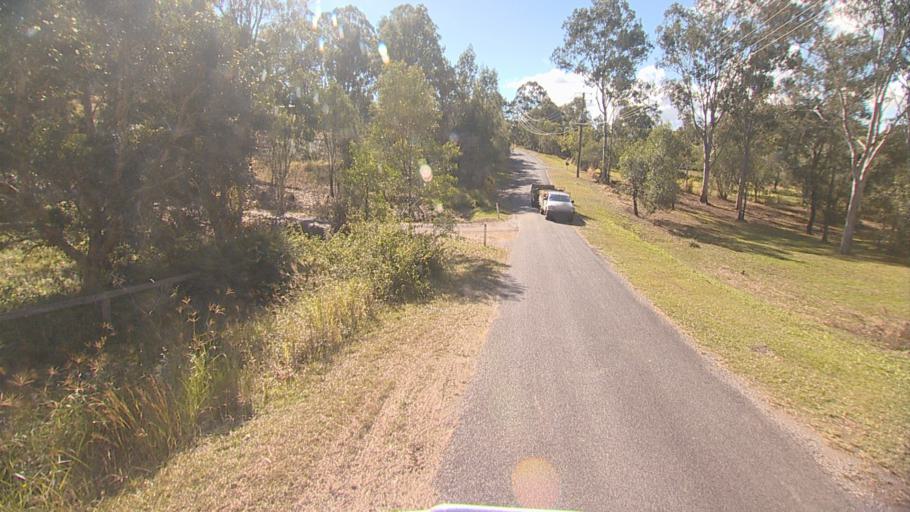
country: AU
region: Queensland
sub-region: Logan
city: Chambers Flat
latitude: -27.8124
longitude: 153.0892
